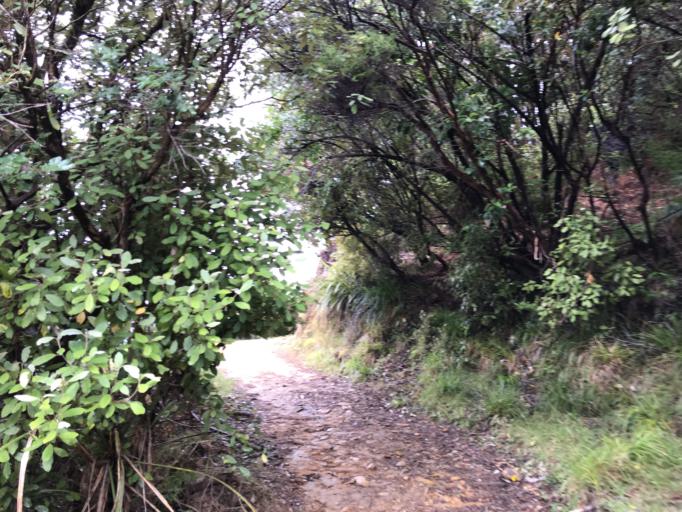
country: NZ
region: Marlborough
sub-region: Marlborough District
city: Picton
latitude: -41.1156
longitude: 174.1630
